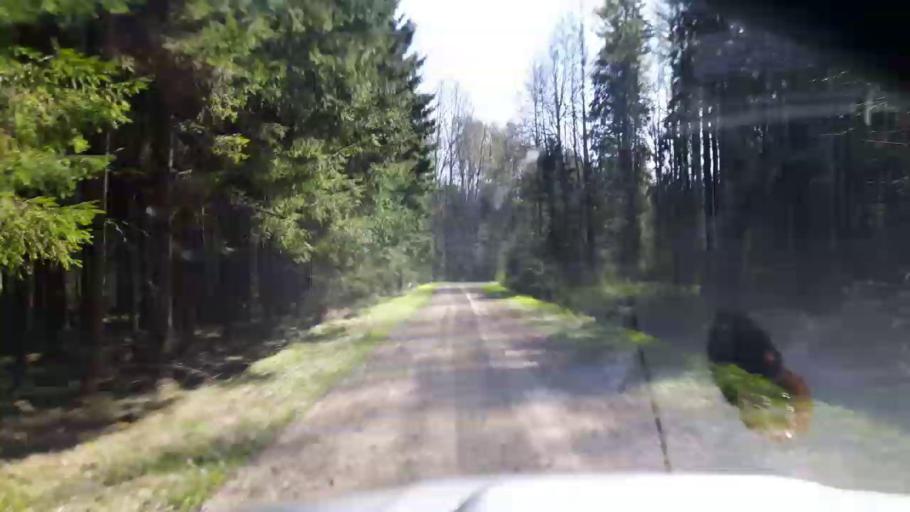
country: EE
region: Paernumaa
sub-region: Tootsi vald
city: Tootsi
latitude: 58.4760
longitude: 24.9153
